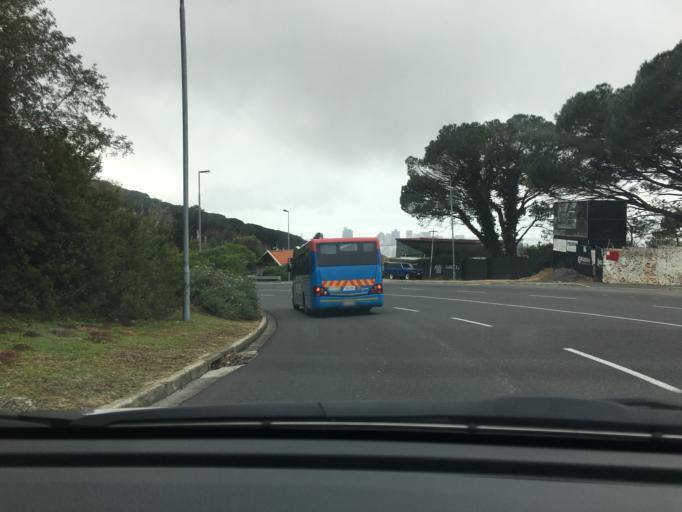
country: ZA
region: Western Cape
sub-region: City of Cape Town
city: Cape Town
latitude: -33.9389
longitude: 18.3978
